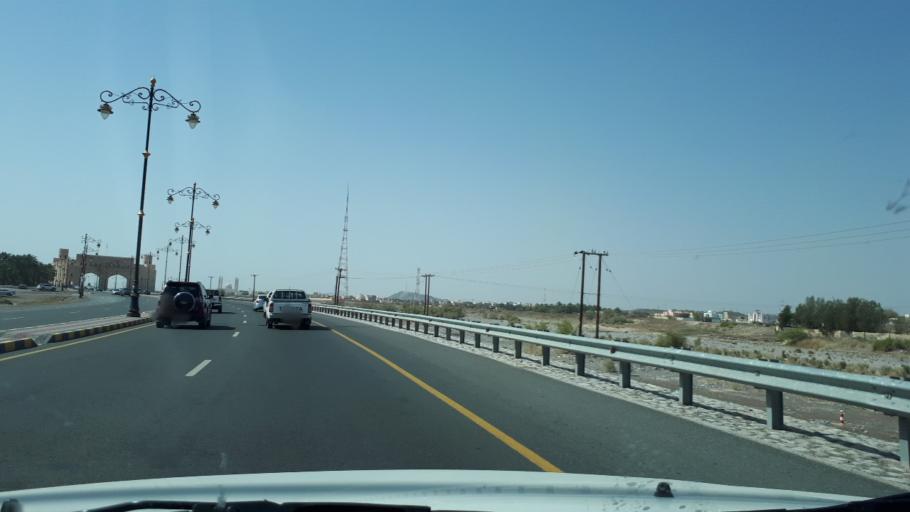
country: OM
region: Muhafazat ad Dakhiliyah
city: Nizwa
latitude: 22.8814
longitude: 57.5254
